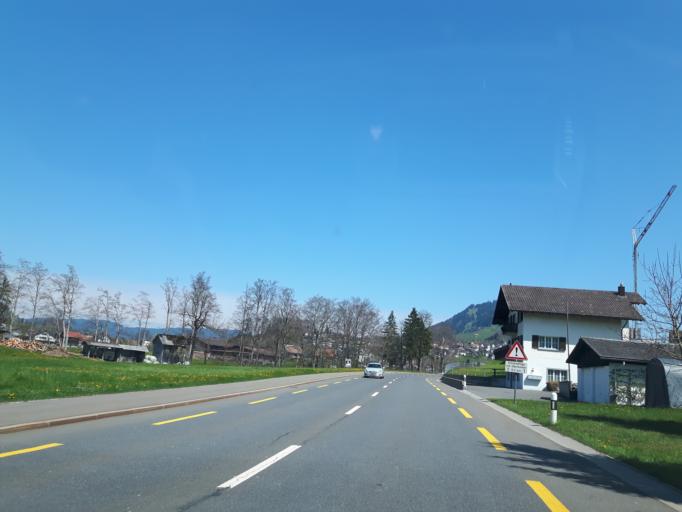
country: CH
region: Schwyz
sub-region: Bezirk Schwyz
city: Sattel
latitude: 47.0754
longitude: 8.6311
